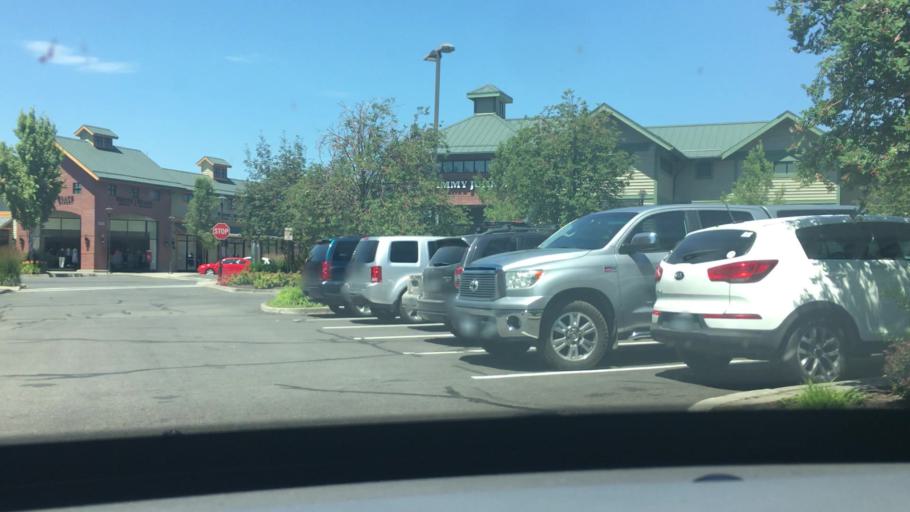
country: US
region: Oregon
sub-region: Deschutes County
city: Bend
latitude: 44.0466
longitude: -121.3143
